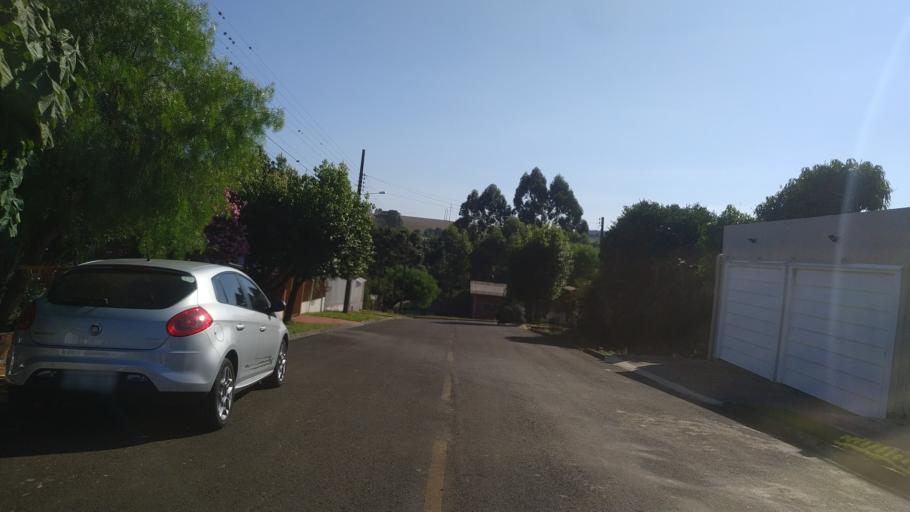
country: BR
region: Santa Catarina
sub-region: Chapeco
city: Chapeco
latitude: -27.0780
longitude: -52.6055
